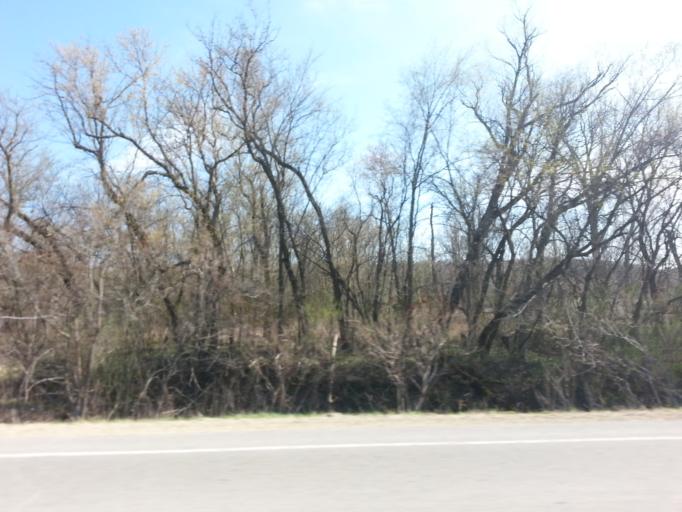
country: US
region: Wisconsin
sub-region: Pierce County
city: Ellsworth
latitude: 44.7762
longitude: -92.5173
